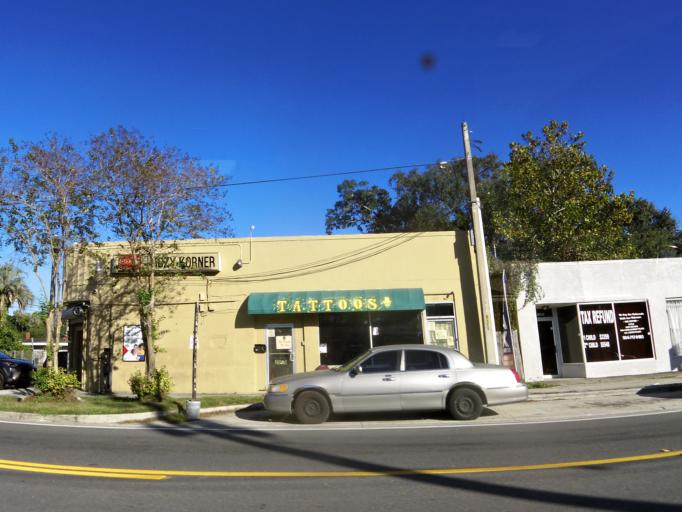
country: US
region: Florida
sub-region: Duval County
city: Jacksonville
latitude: 30.3480
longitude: -81.6757
